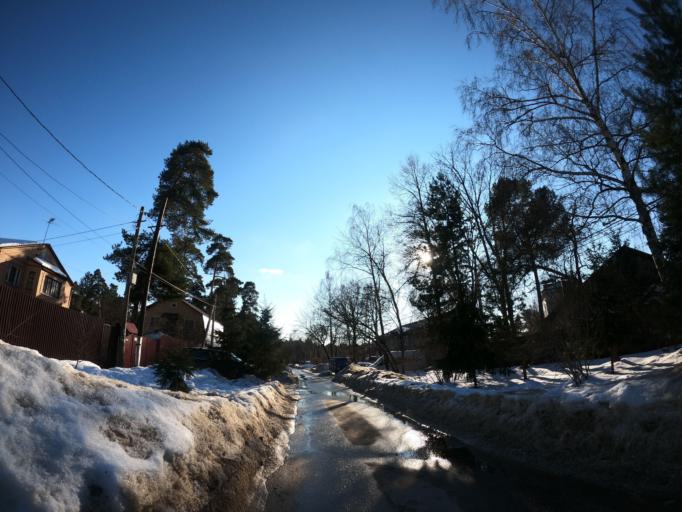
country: RU
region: Moskovskaya
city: Kraskovo
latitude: 55.6423
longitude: 37.9940
